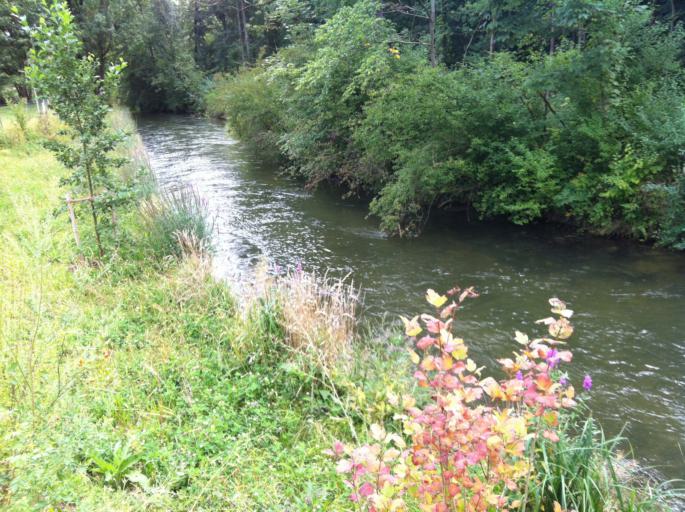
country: DE
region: Bavaria
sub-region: Upper Bavaria
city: Unterfoehring
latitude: 48.2005
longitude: 11.6280
